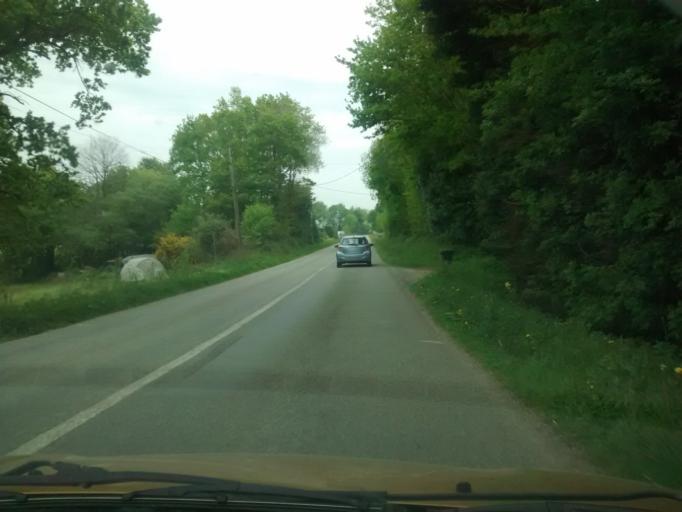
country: FR
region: Brittany
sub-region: Departement du Morbihan
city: Berric
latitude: 47.6357
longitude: -2.5154
